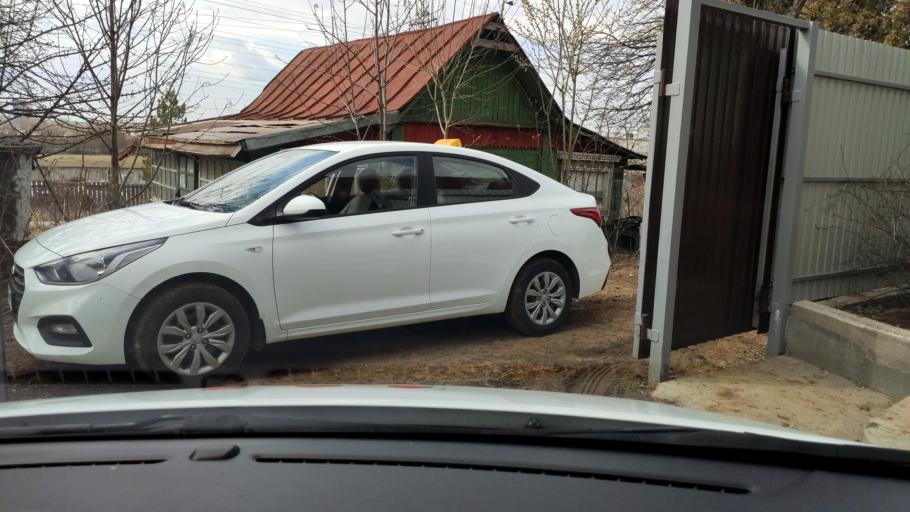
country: RU
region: Tatarstan
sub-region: Gorod Kazan'
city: Kazan
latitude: 55.8190
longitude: 49.2117
